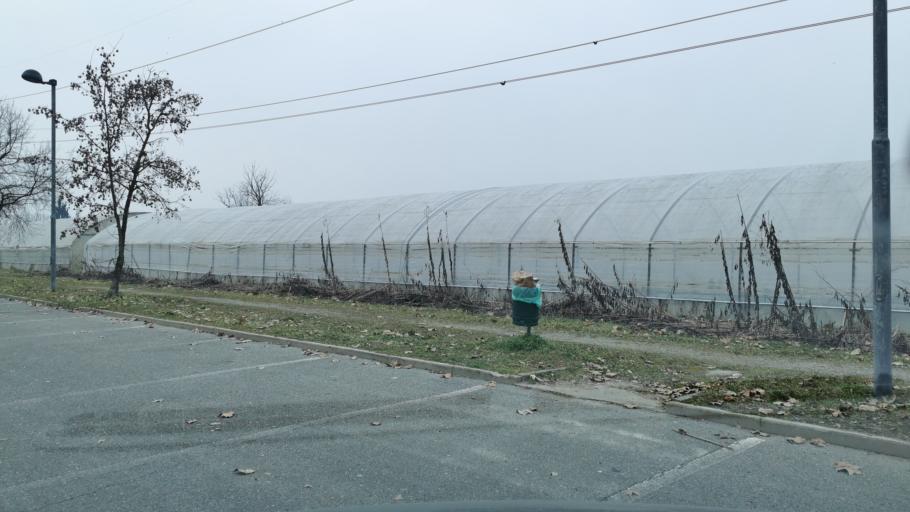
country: IT
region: Piedmont
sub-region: Provincia di Torino
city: San Mauro Torinese
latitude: 45.1148
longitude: 7.7626
